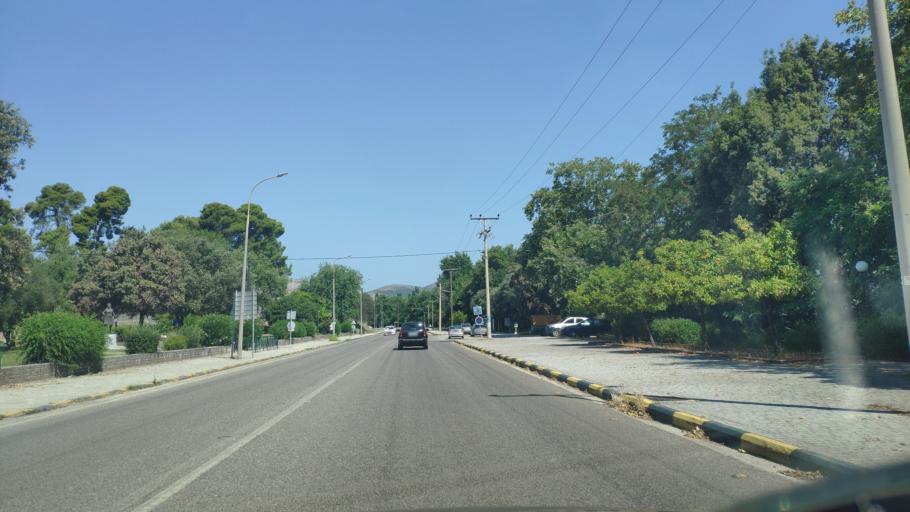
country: GR
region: Epirus
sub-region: Nomos Artas
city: Arta
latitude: 39.1648
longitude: 20.9905
